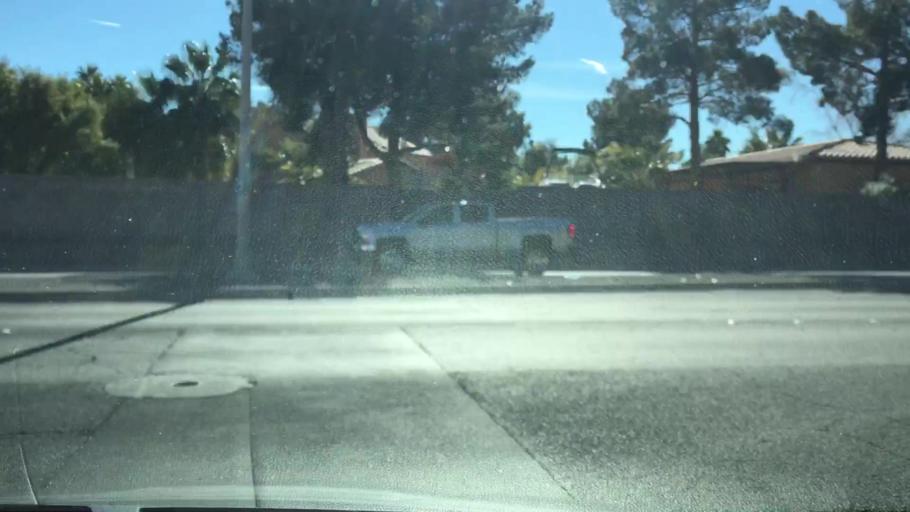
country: US
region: Nevada
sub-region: Clark County
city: Whitney
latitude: 36.0563
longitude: -115.0637
